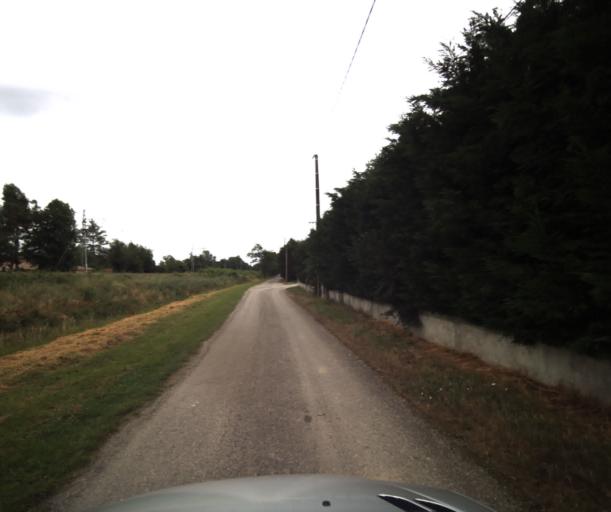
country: FR
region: Midi-Pyrenees
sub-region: Departement de la Haute-Garonne
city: Labarthe-sur-Leze
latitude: 43.4540
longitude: 1.4140
